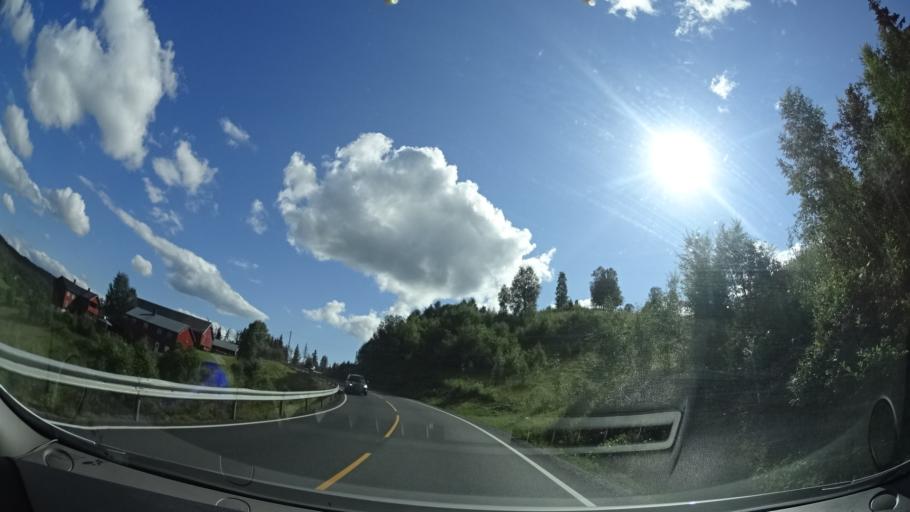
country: NO
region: Sor-Trondelag
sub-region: Snillfjord
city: Krokstadora
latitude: 63.2386
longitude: 9.5932
